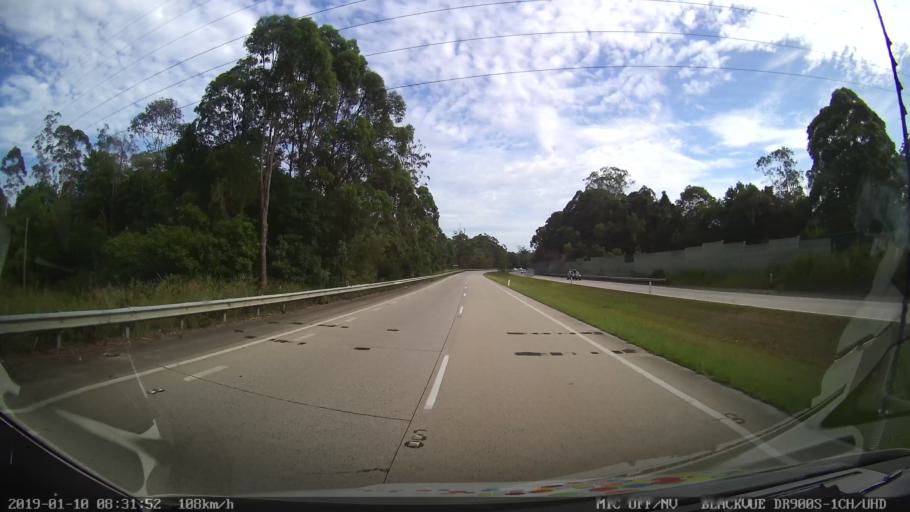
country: AU
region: New South Wales
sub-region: Coffs Harbour
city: Boambee
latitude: -30.3506
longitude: 153.0649
